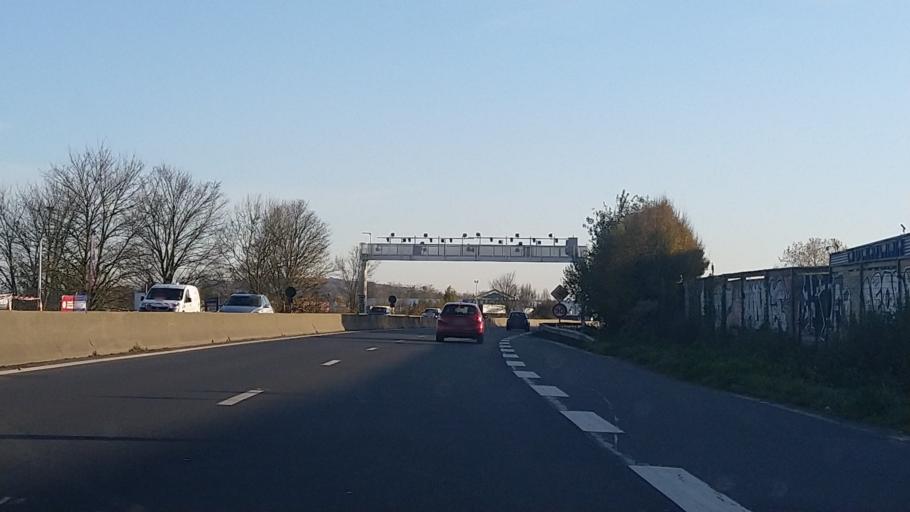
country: FR
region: Ile-de-France
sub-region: Departement du Val-d'Oise
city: Moisselles
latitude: 49.0412
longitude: 2.3421
